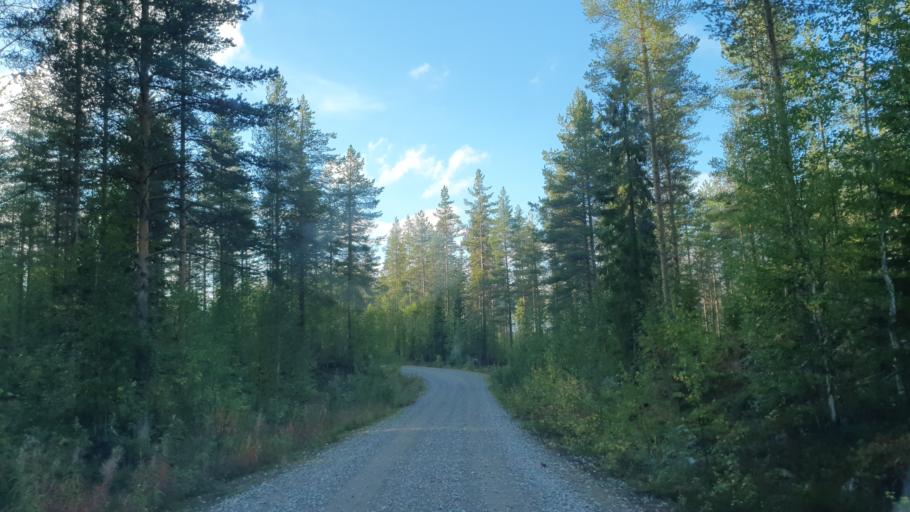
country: FI
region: Kainuu
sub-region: Kehys-Kainuu
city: Kuhmo
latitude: 64.3384
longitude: 29.9854
